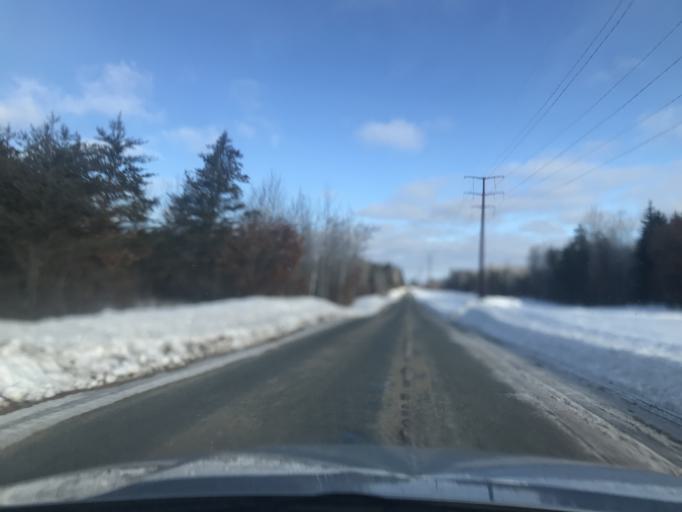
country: US
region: Wisconsin
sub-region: Marinette County
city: Niagara
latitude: 45.5917
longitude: -87.9769
